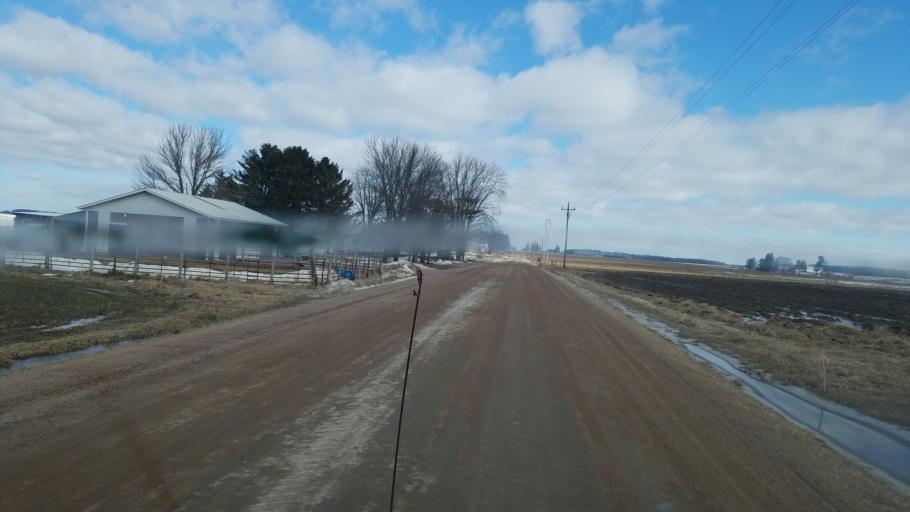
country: US
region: Wisconsin
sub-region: Clark County
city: Loyal
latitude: 44.6624
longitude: -90.4356
